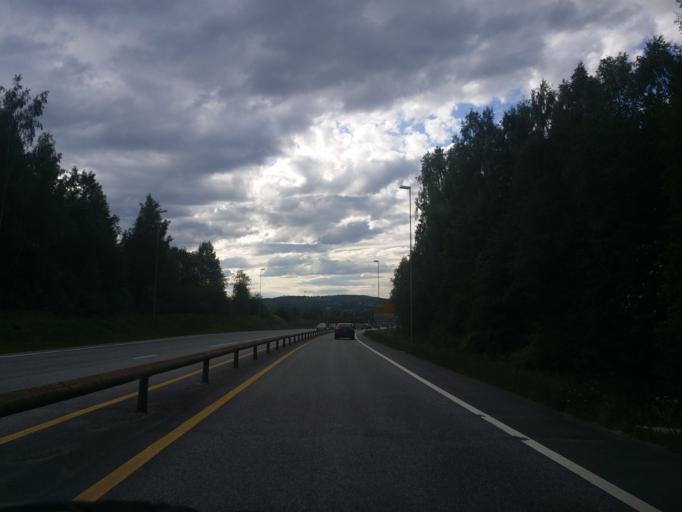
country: NO
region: Hedmark
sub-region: Hamar
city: Hamar
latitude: 60.7829
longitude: 11.1346
